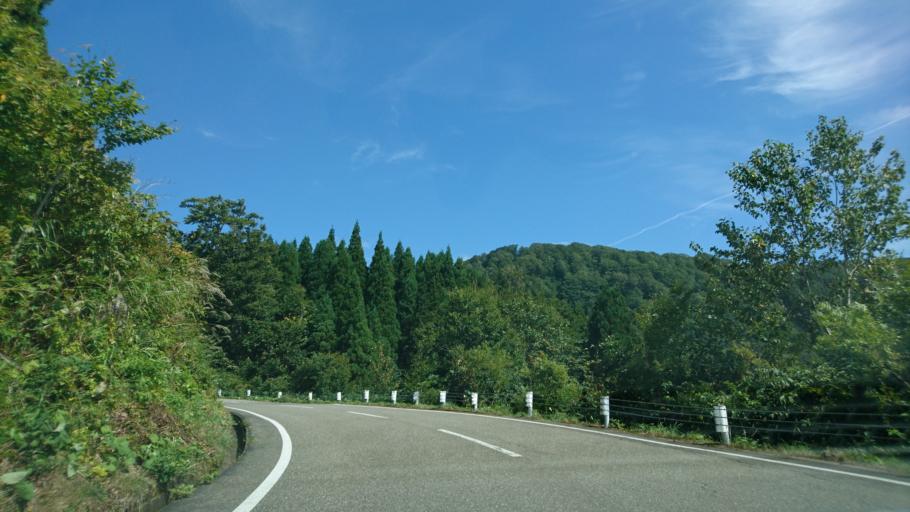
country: JP
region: Akita
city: Yuzawa
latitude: 38.9587
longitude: 140.7134
